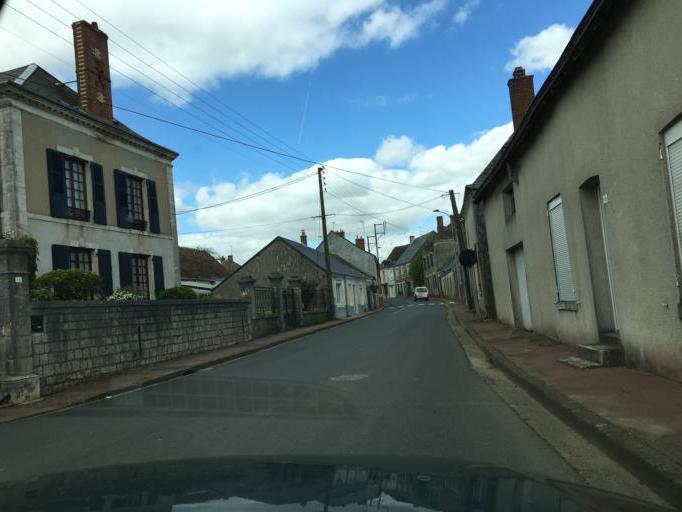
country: FR
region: Centre
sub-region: Departement du Loir-et-Cher
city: Oucques
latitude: 47.8218
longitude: 1.3942
